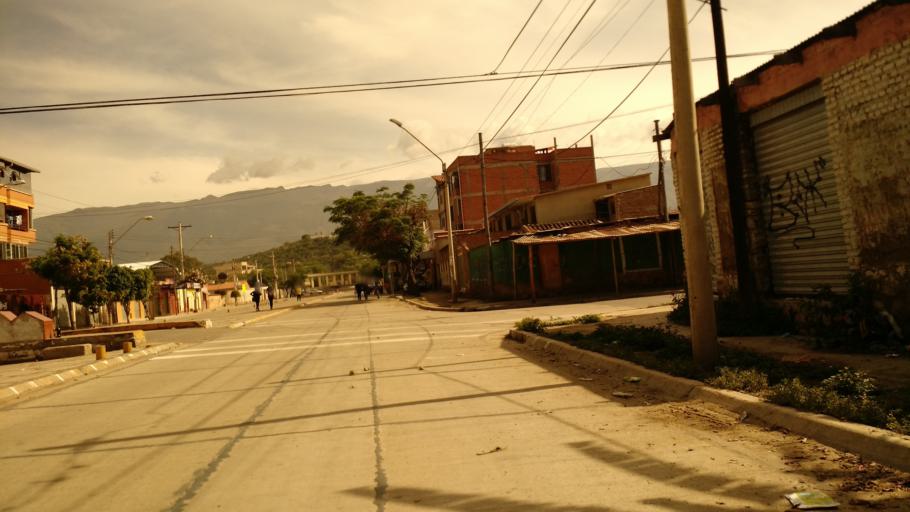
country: BO
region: Cochabamba
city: Cochabamba
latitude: -17.4155
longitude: -66.1591
